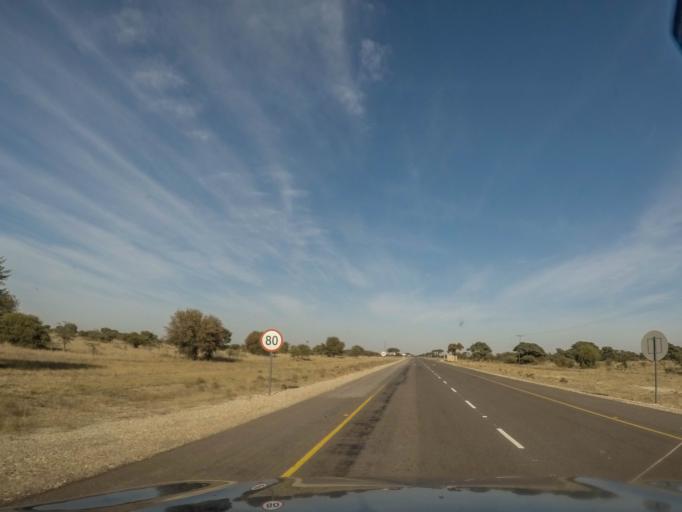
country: BW
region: South East
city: Janeng
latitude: -25.5601
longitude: 25.3090
